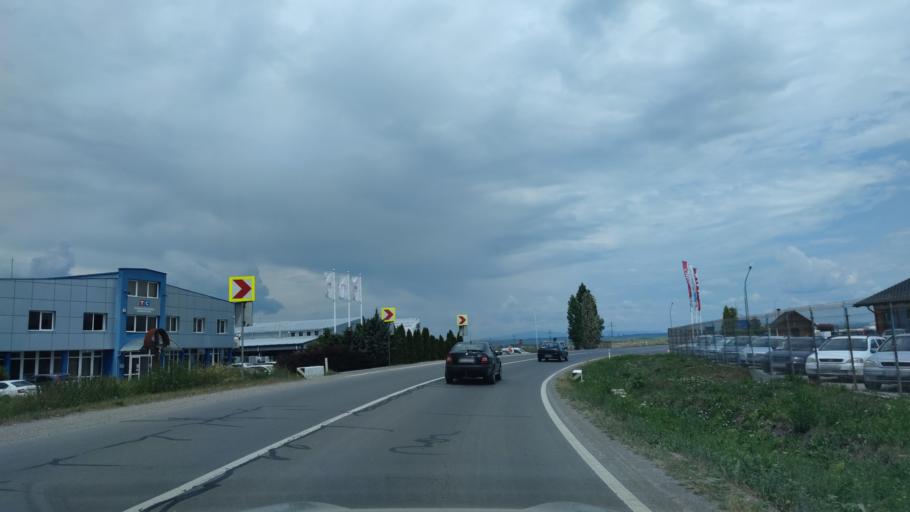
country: RO
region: Harghita
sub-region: Comuna Ciceu
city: Ciceu
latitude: 46.3839
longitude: 25.7982
